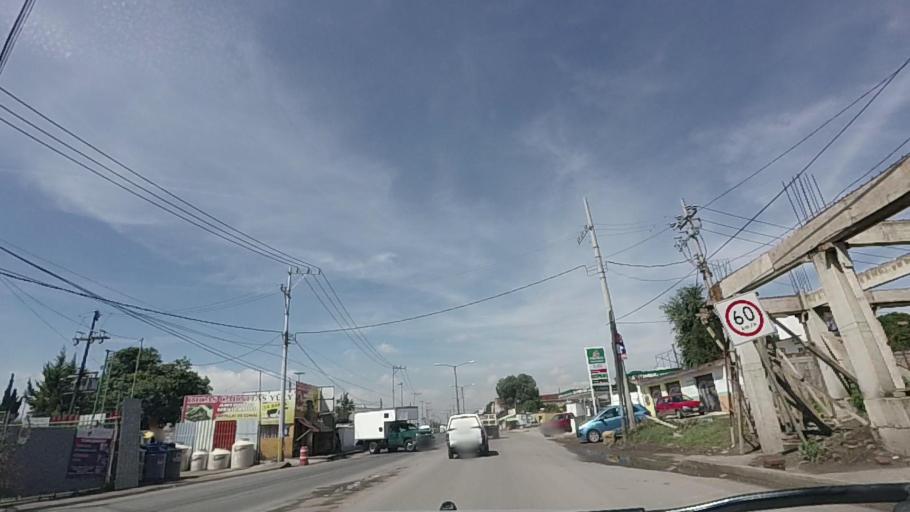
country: MX
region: Mexico
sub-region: Cuautitlan
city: San Jose del Puente
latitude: 19.7199
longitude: -99.1920
